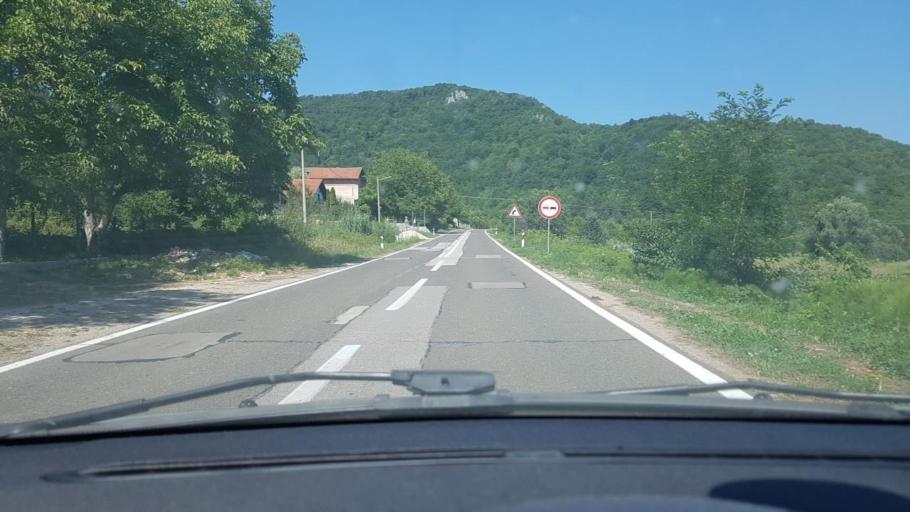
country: BA
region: Federation of Bosnia and Herzegovina
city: Bihac
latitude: 44.7498
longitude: 15.9270
